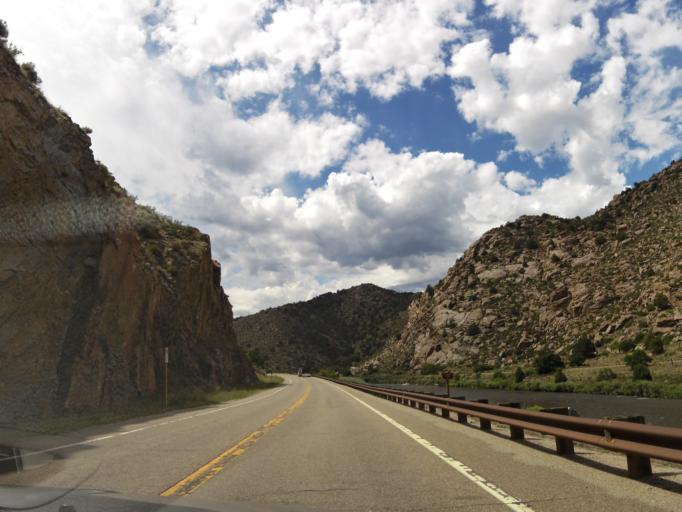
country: US
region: Colorado
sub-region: Custer County
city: Westcliffe
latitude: 38.3907
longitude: -105.6481
